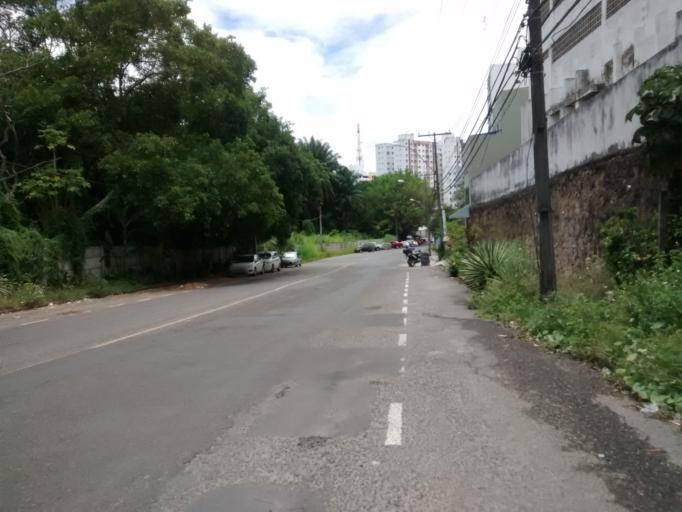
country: BR
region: Bahia
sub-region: Salvador
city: Salvador
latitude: -12.9746
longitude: -38.4412
